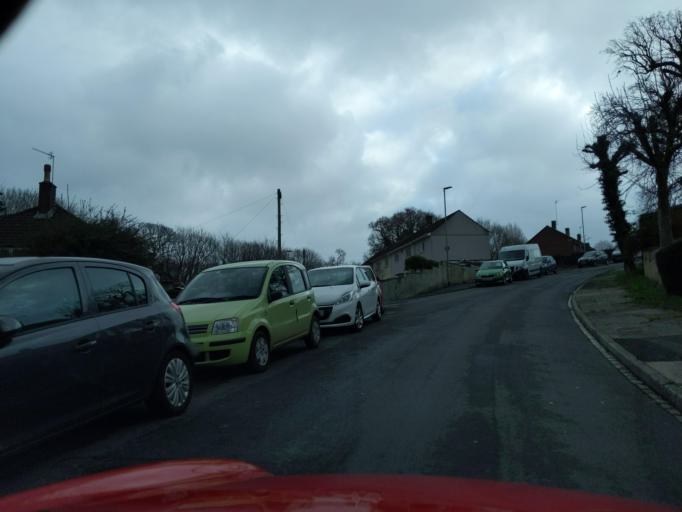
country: GB
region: England
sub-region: Plymouth
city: Plymouth
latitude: 50.4017
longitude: -4.1434
